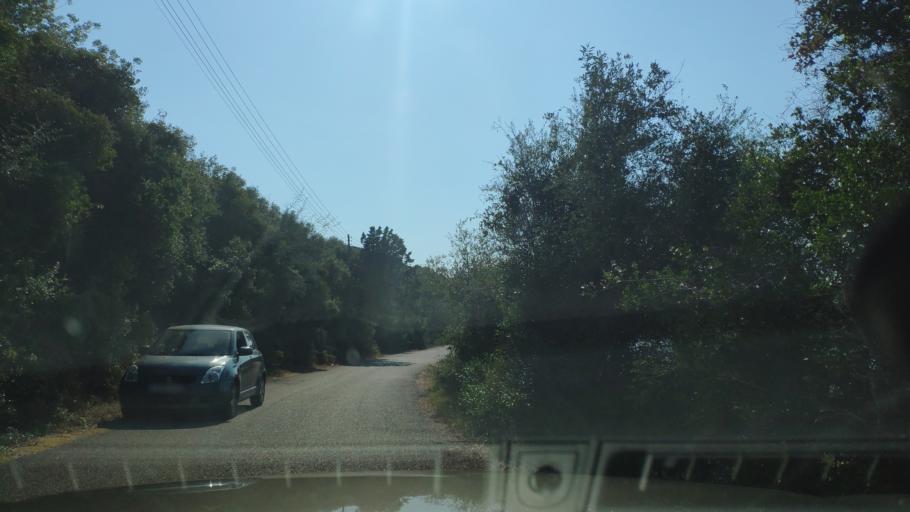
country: GR
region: West Greece
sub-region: Nomos Aitolias kai Akarnanias
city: Amfilochia
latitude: 38.9045
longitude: 21.1140
